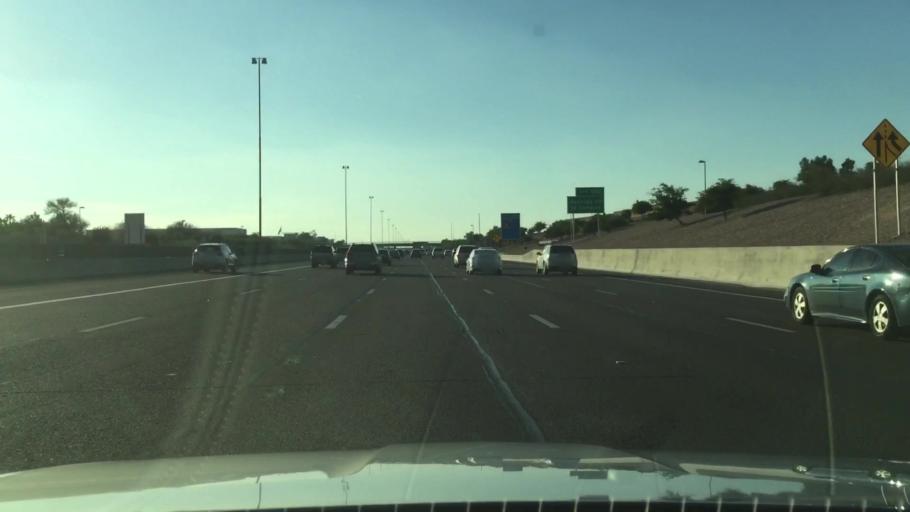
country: US
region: Arizona
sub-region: Maricopa County
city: Gilbert
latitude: 33.3854
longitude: -111.8062
